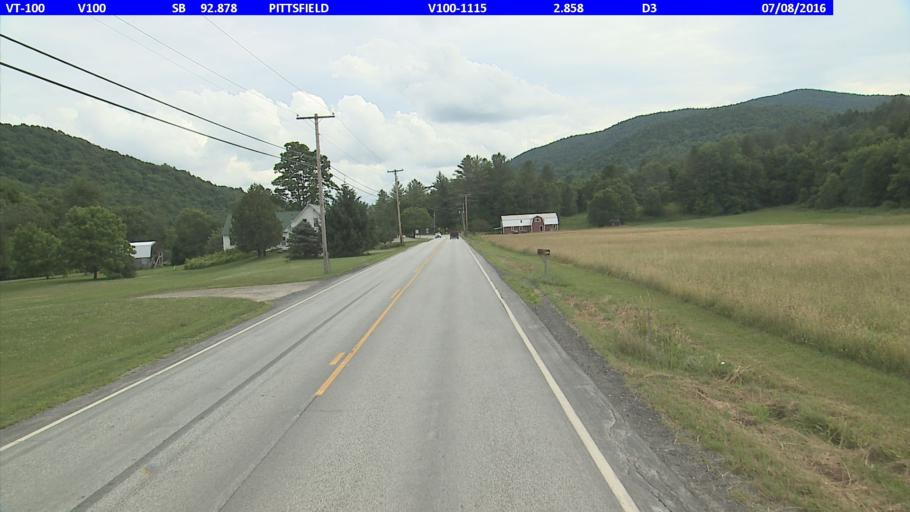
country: US
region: Vermont
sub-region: Rutland County
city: Rutland
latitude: 43.7581
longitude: -72.8198
